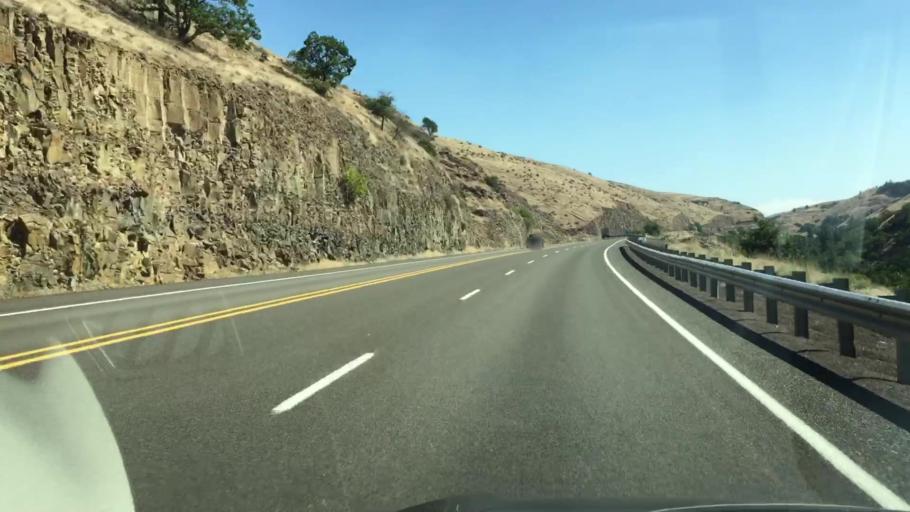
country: US
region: Oregon
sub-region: Wasco County
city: The Dalles
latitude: 45.2937
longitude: -121.1761
